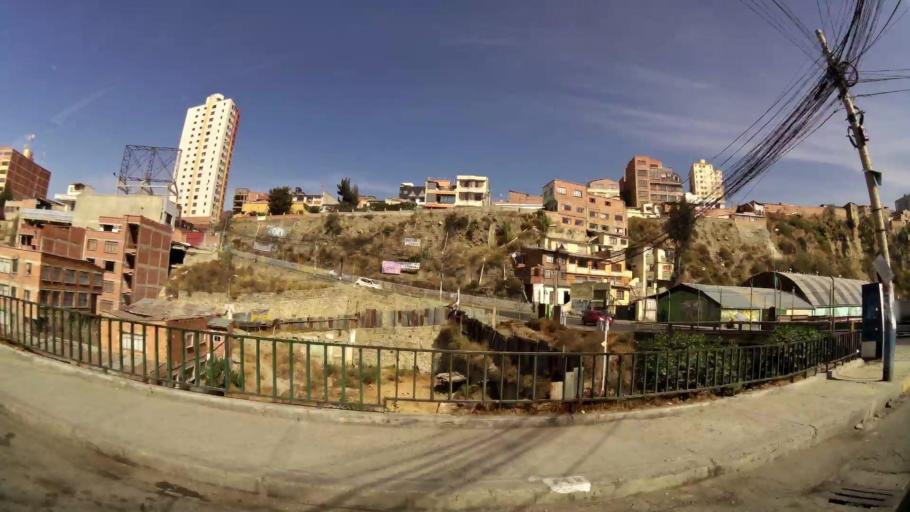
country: BO
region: La Paz
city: La Paz
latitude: -16.4963
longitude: -68.1179
